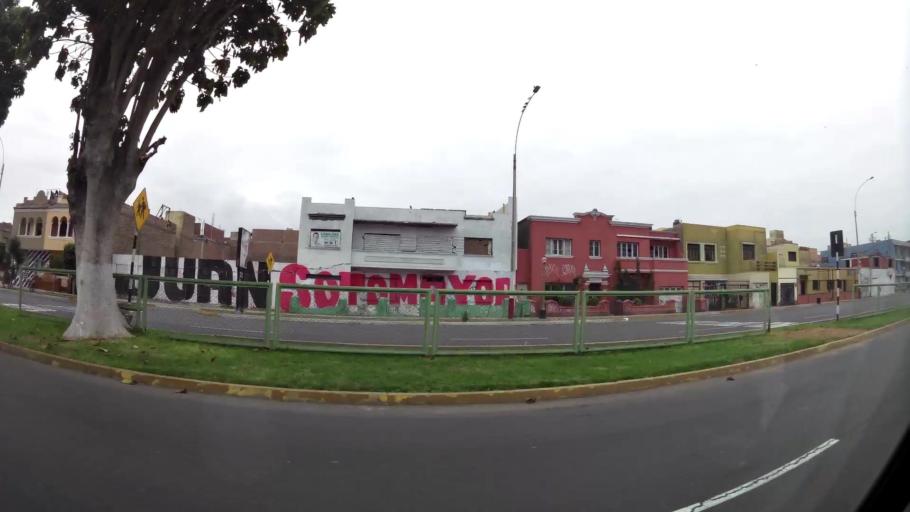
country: PE
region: Callao
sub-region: Callao
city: Callao
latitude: -12.0571
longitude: -77.1312
